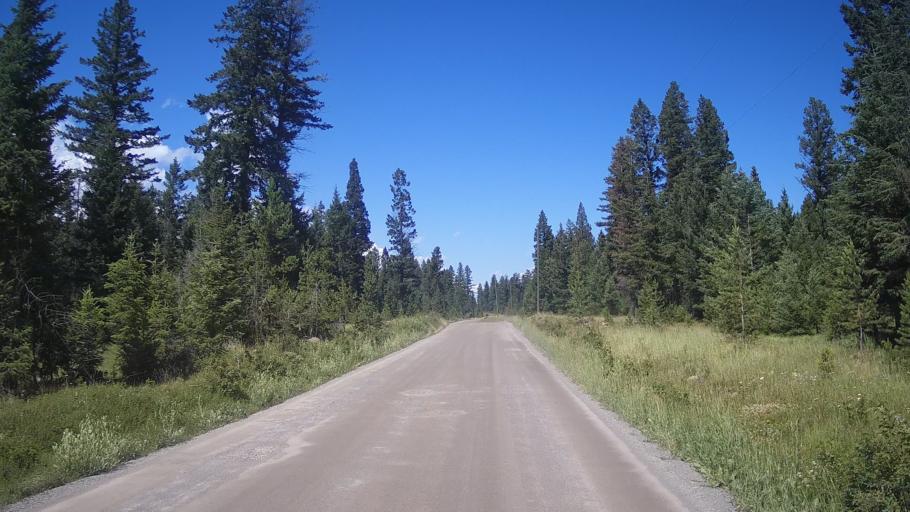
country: CA
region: British Columbia
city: Cache Creek
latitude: 51.2082
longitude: -121.5979
